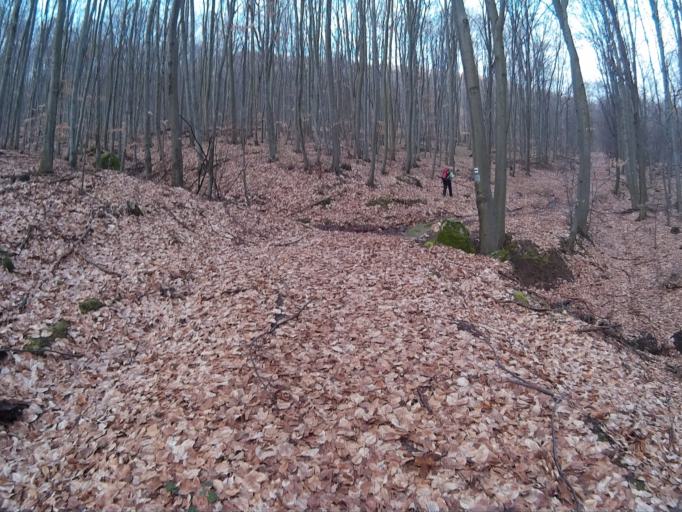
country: HU
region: Borsod-Abauj-Zemplen
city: Tolcsva
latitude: 48.3543
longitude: 21.4914
